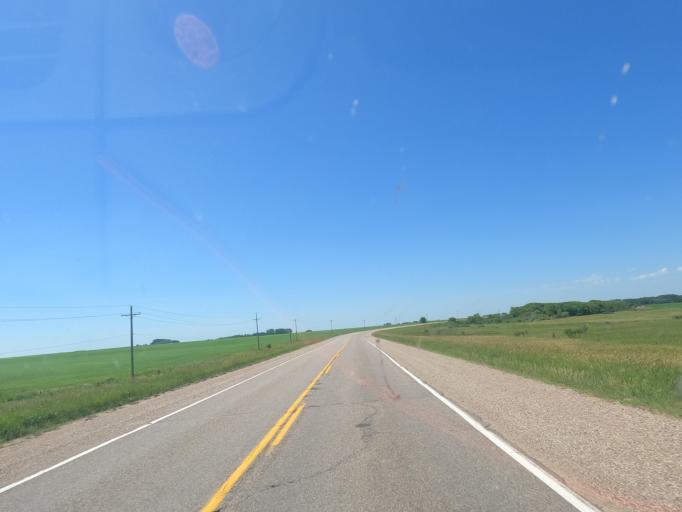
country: CA
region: Manitoba
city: Souris
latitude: 49.6204
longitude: -100.2871
